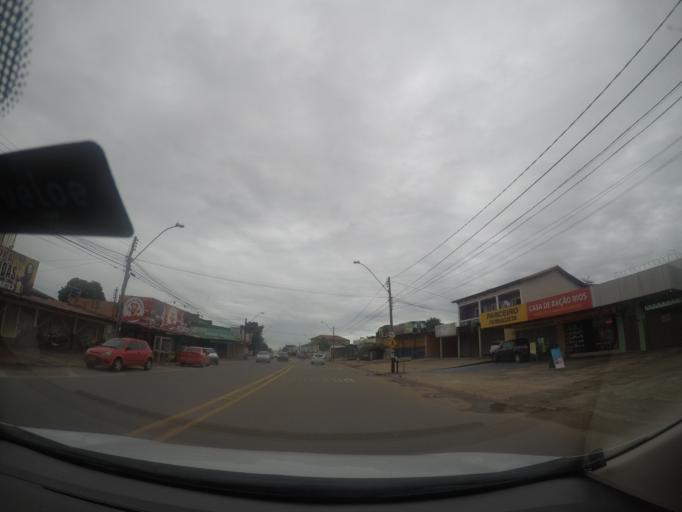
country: BR
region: Goias
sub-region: Goiania
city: Goiania
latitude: -16.6163
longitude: -49.2940
